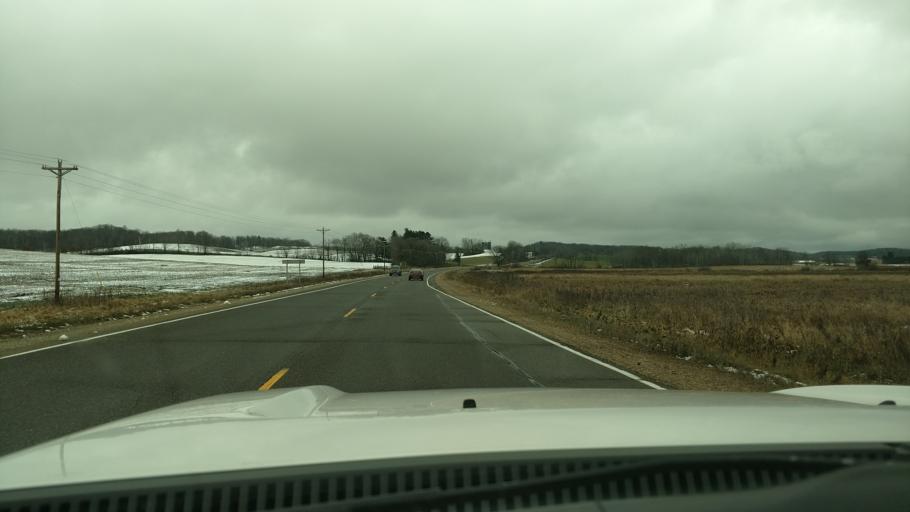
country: US
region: Wisconsin
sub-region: Dunn County
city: Boyceville
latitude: 45.1401
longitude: -91.9689
